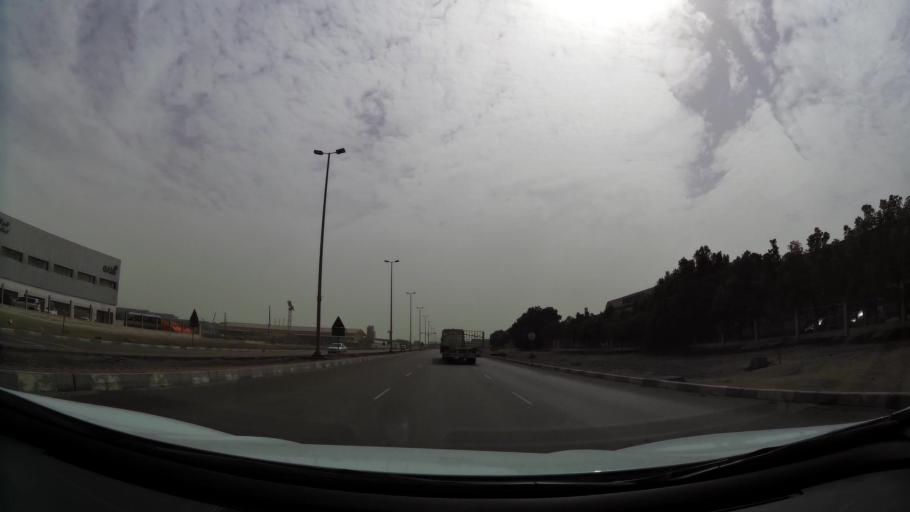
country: AE
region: Abu Dhabi
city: Abu Dhabi
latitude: 24.3271
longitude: 54.4736
